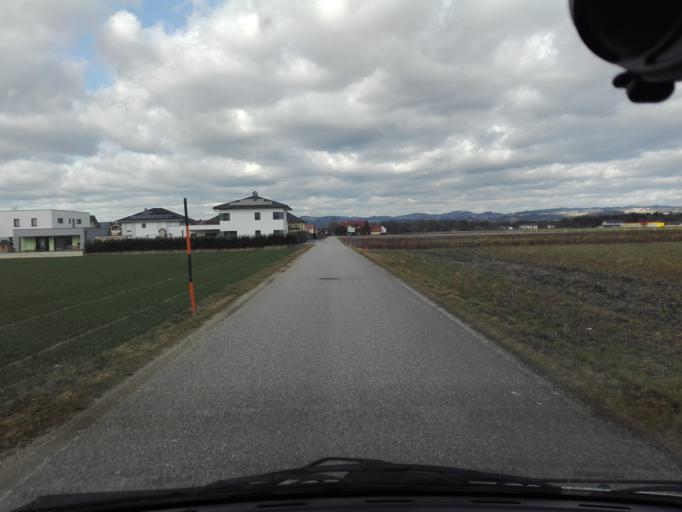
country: AT
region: Upper Austria
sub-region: Politischer Bezirk Perg
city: Perg
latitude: 48.1935
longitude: 14.6829
